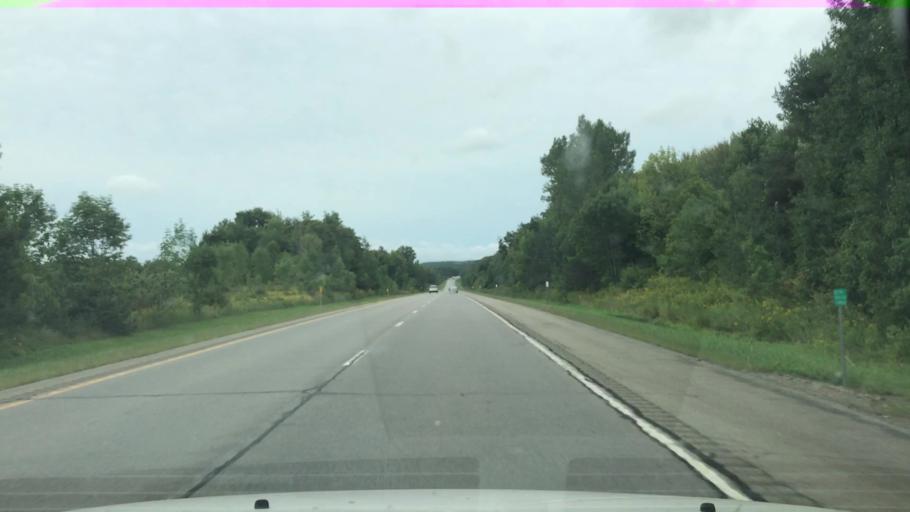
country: US
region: New York
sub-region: Erie County
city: Springville
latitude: 42.5842
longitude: -78.7305
